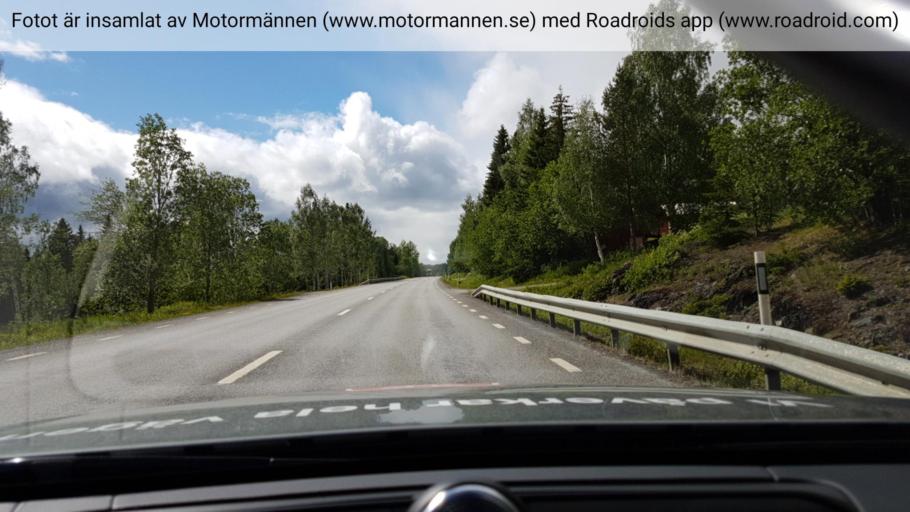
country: SE
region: Jaemtland
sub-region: Are Kommun
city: Jarpen
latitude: 63.3105
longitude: 13.6756
